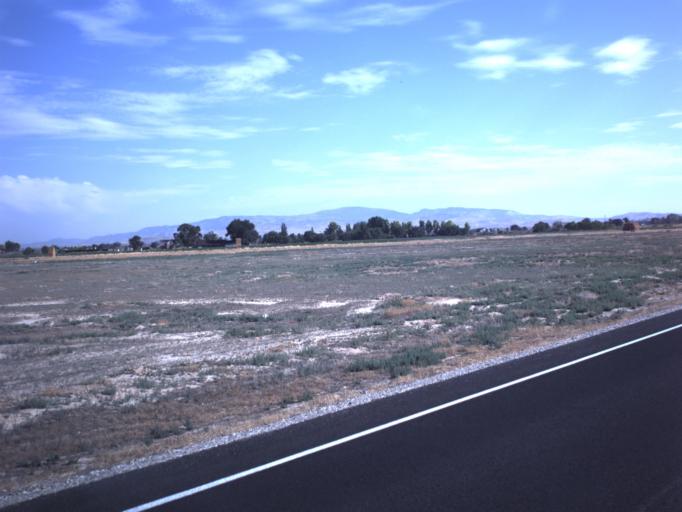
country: US
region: Utah
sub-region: Sanpete County
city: Centerfield
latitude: 39.0398
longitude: -111.8316
